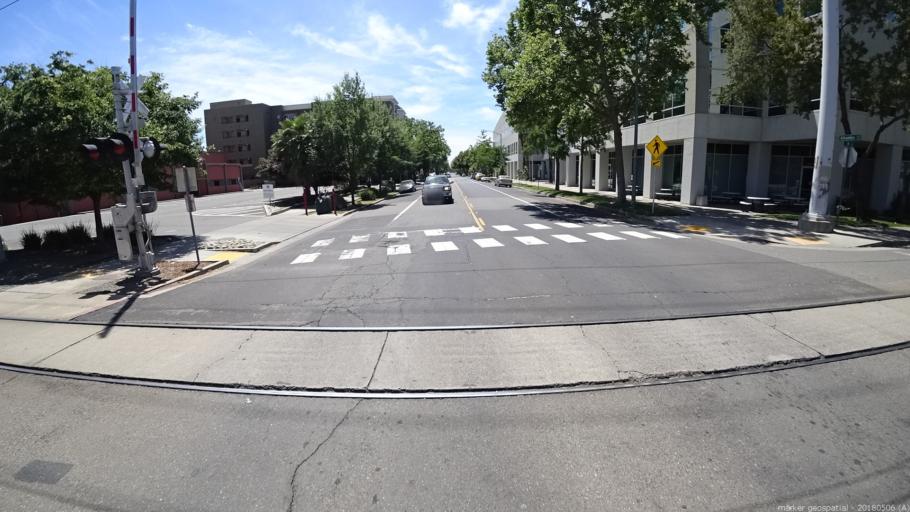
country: US
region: California
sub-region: Sacramento County
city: Sacramento
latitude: 38.5639
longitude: -121.4692
